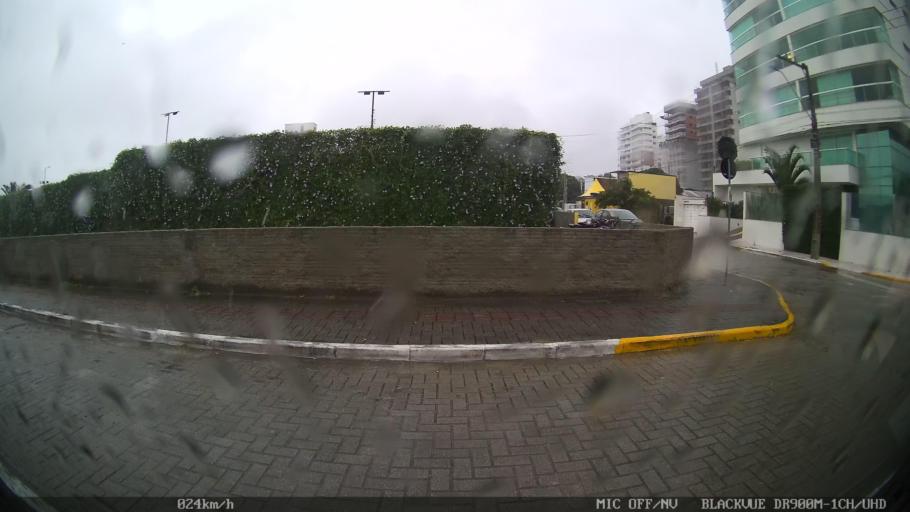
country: BR
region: Santa Catarina
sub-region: Balneario Camboriu
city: Balneario Camboriu
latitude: -26.9444
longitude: -48.6296
